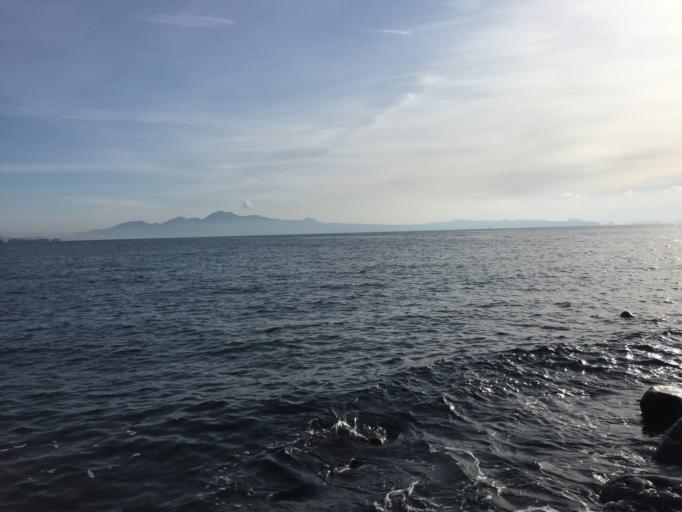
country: JP
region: Nagasaki
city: Nagasaki-shi
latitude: 32.7268
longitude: 129.9429
